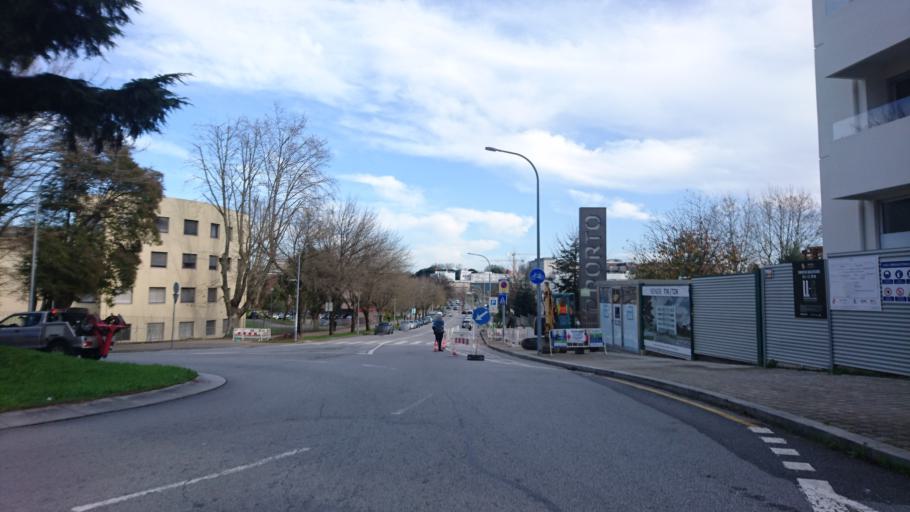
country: PT
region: Porto
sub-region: Matosinhos
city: Sao Mamede de Infesta
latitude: 41.1768
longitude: -8.6078
